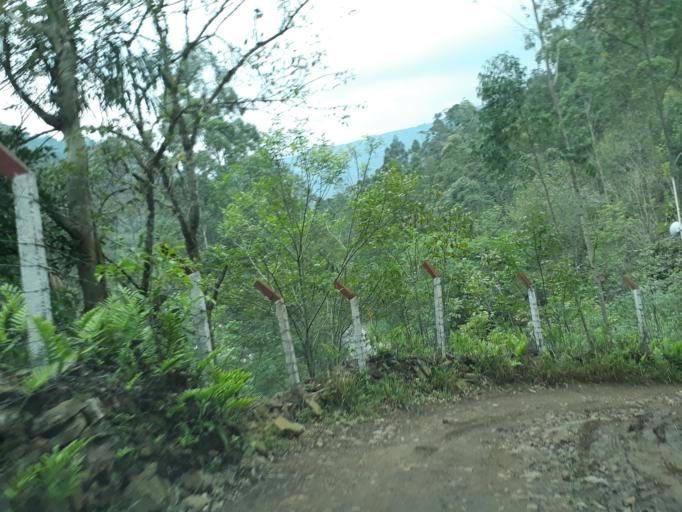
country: CO
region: Cundinamarca
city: Manta
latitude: 5.0613
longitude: -73.5263
